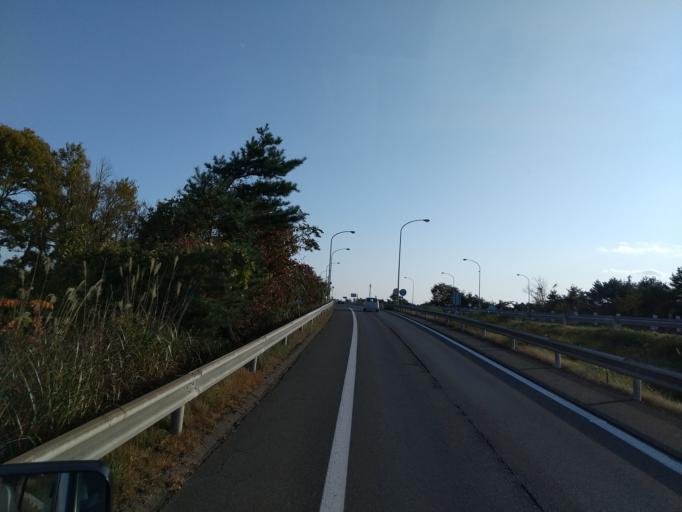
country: JP
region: Iwate
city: Morioka-shi
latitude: 39.6513
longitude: 141.1235
